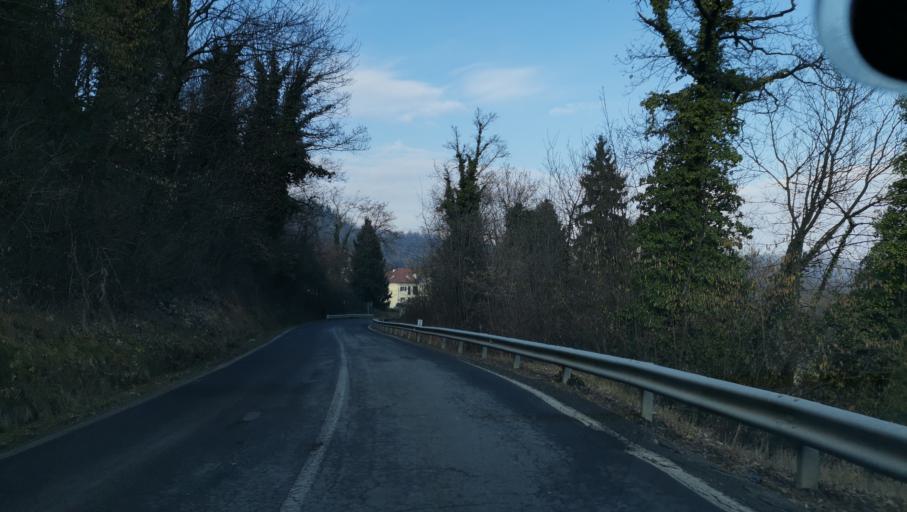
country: IT
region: Piedmont
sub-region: Provincia di Torino
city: Gassino Torinese
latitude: 45.1027
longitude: 7.8429
